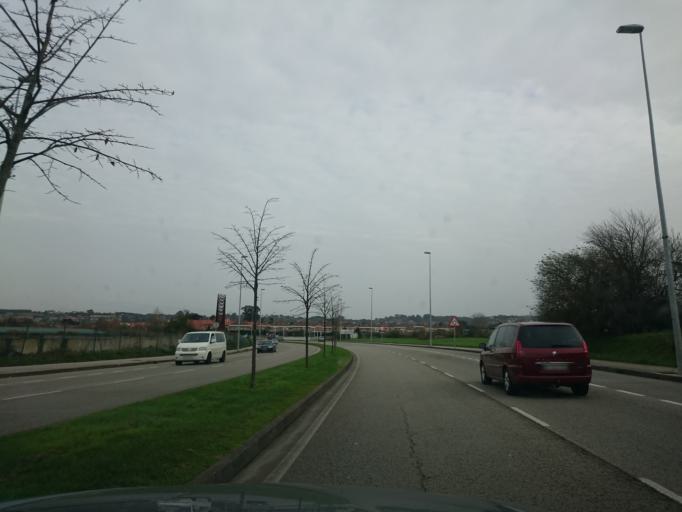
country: ES
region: Asturias
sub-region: Province of Asturias
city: Gijon
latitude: 43.5258
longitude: -5.6372
